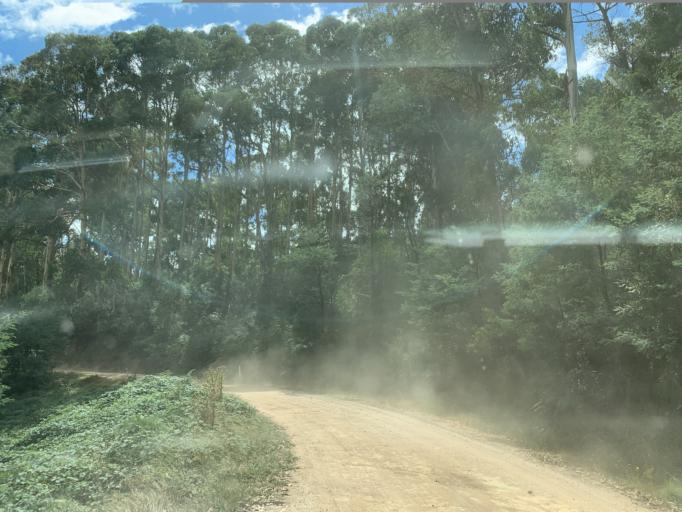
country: AU
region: Victoria
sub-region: Mansfield
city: Mansfield
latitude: -37.0981
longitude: 146.5134
